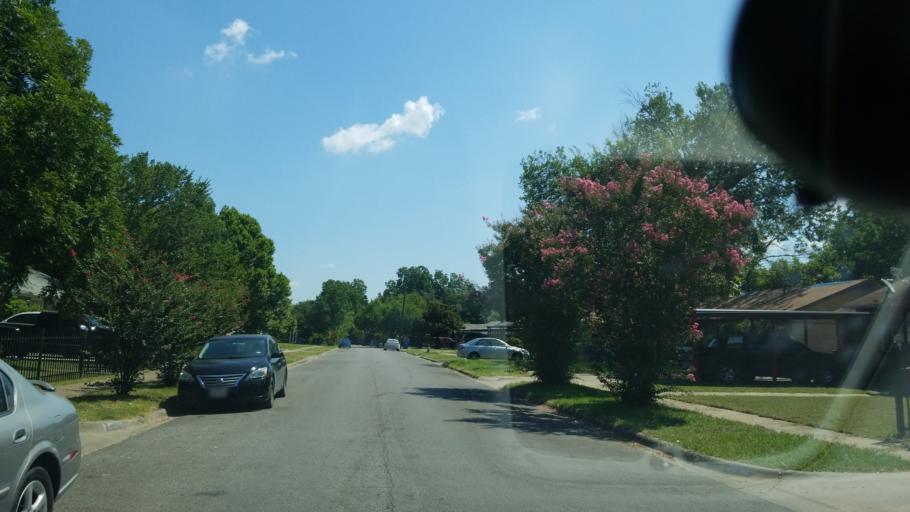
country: US
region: Texas
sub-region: Dallas County
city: Cockrell Hill
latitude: 32.7141
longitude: -96.8354
